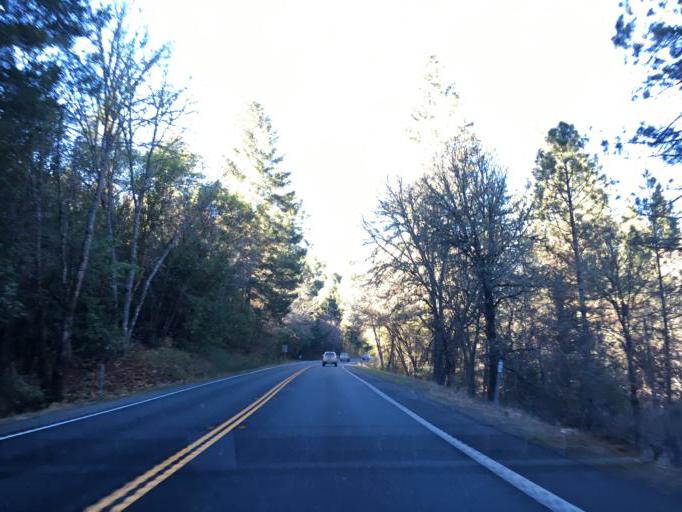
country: US
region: California
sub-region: Mendocino County
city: Brooktrails
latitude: 39.4884
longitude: -123.3620
